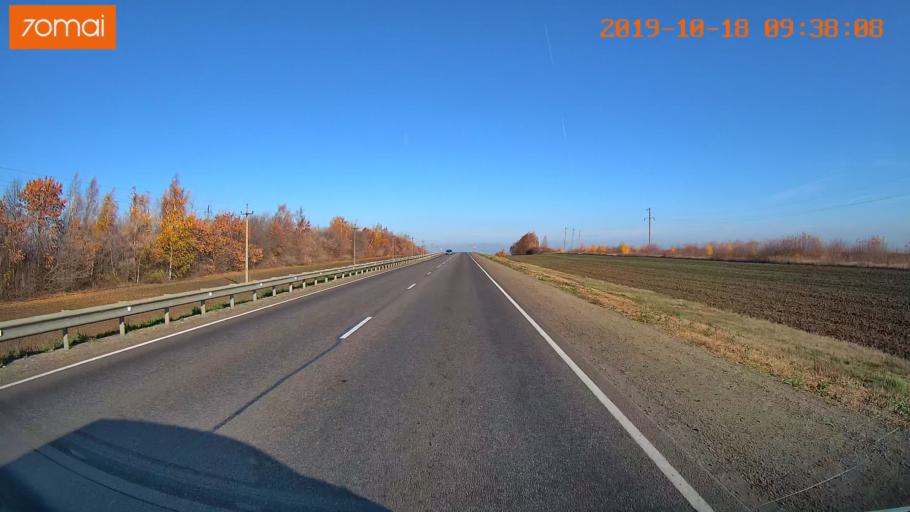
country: RU
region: Tula
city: Yefremov
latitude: 53.2331
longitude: 38.1383
